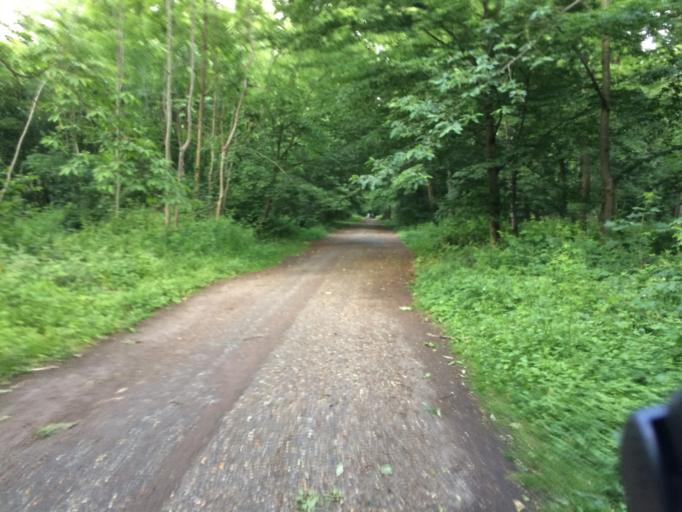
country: FR
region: Ile-de-France
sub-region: Departement de l'Essonne
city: Igny
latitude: 48.7564
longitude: 2.2440
